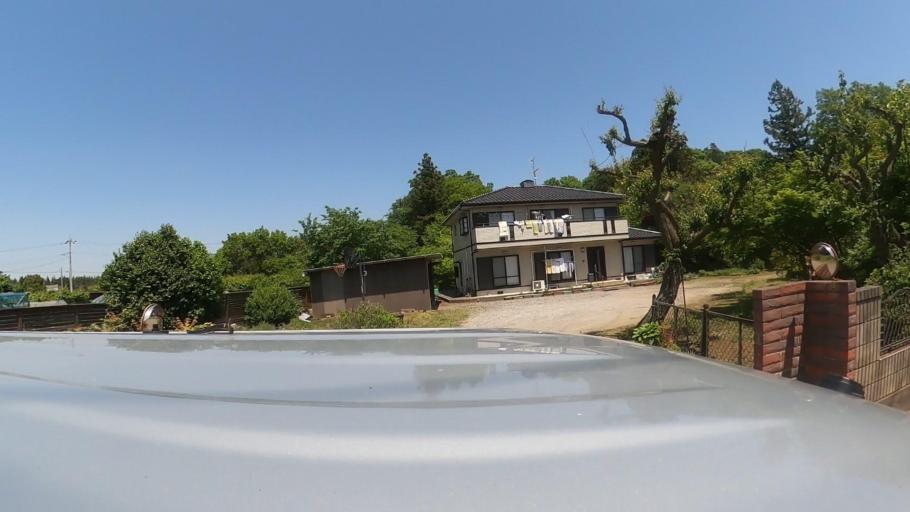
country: JP
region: Ibaraki
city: Ushiku
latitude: 36.0189
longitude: 140.1066
